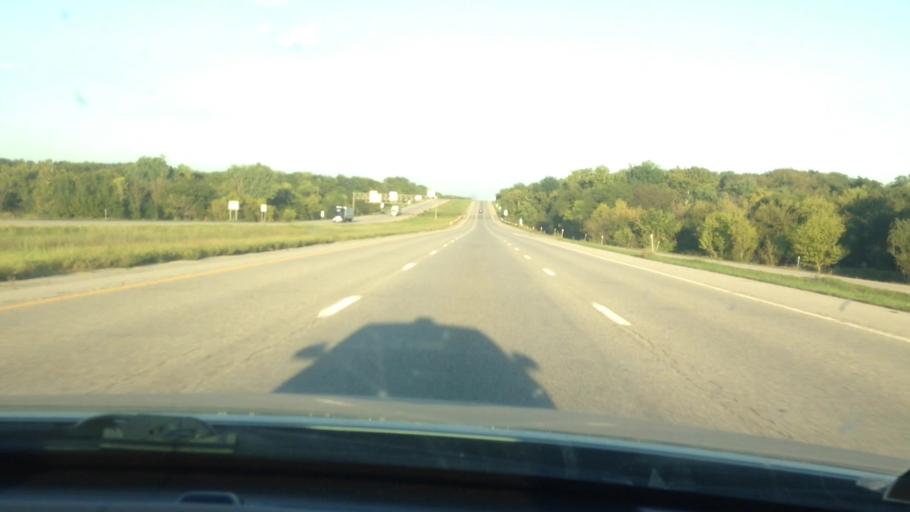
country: US
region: Missouri
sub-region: Platte County
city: Weatherby Lake
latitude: 39.3074
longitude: -94.6473
